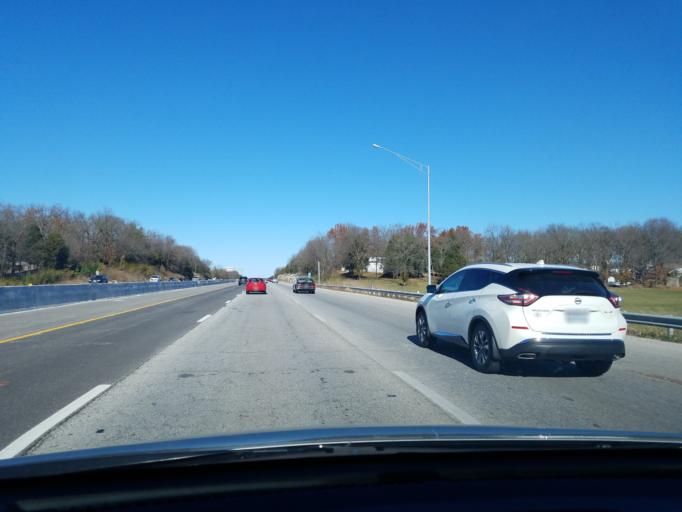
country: US
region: Missouri
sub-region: Christian County
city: Nixa
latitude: 37.1051
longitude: -93.2329
